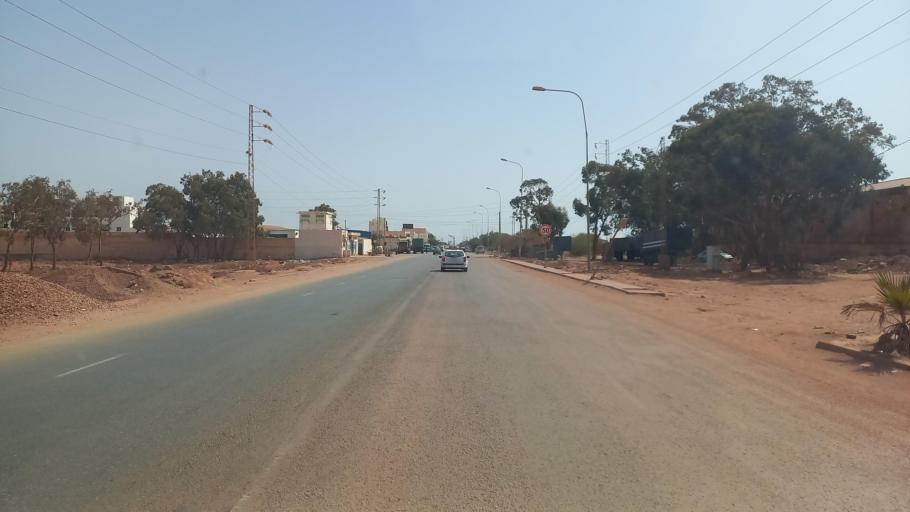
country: TN
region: Madanin
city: Medenine
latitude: 33.3451
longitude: 10.5147
